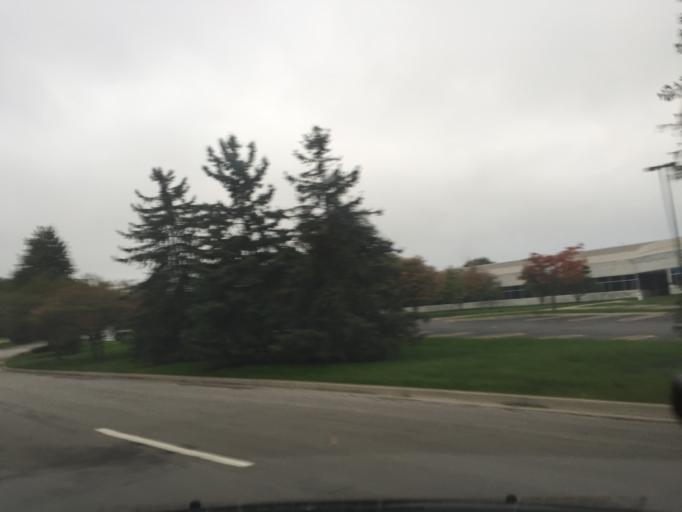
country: US
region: Michigan
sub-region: Oakland County
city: Auburn Hills
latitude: 42.6470
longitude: -83.2421
